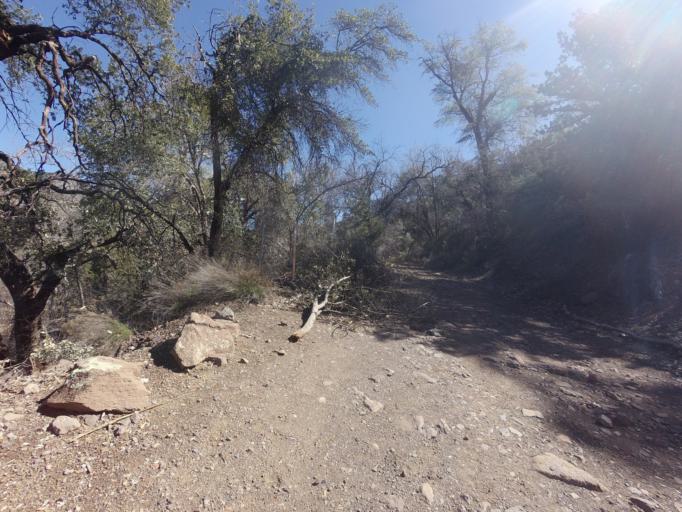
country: US
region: Arizona
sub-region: Gila County
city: Pine
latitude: 34.4049
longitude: -111.6113
